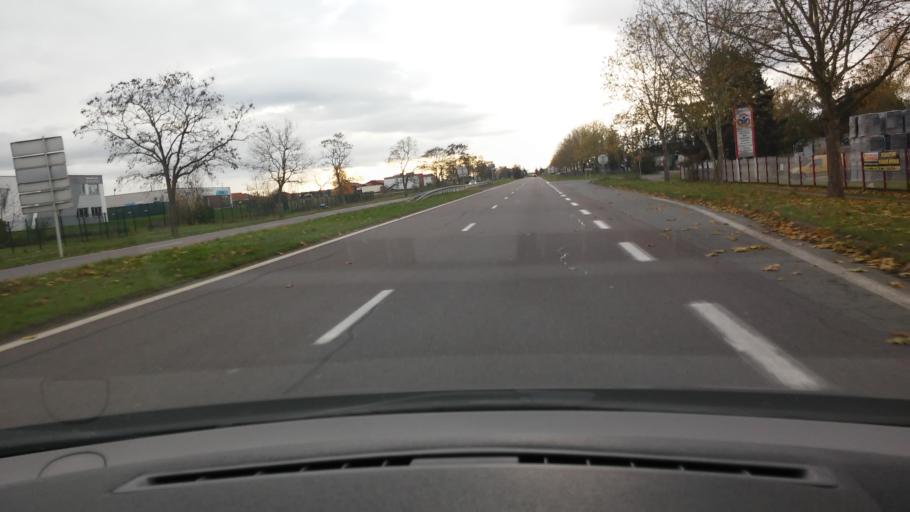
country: FR
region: Lorraine
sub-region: Departement de la Moselle
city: Ennery
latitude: 49.2248
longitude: 6.2104
